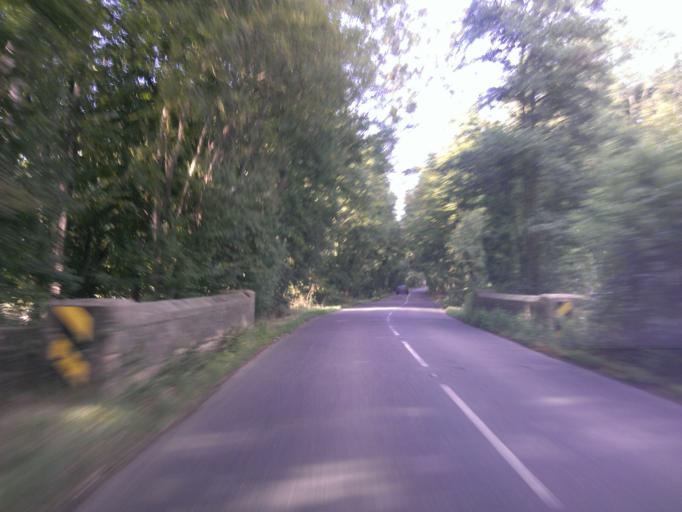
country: GB
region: England
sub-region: Kent
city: Tonbridge
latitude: 51.2063
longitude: 0.2235
